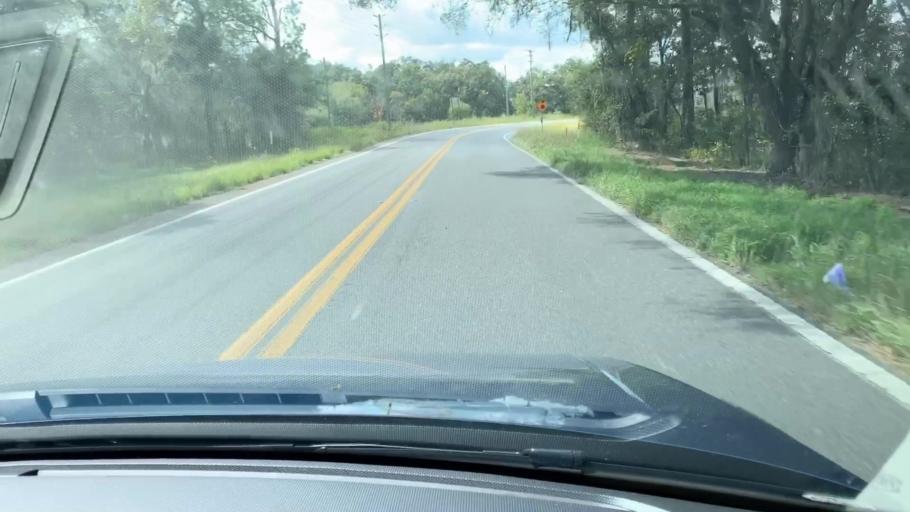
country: US
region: Florida
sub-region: Polk County
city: Winston
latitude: 28.0266
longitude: -82.0537
